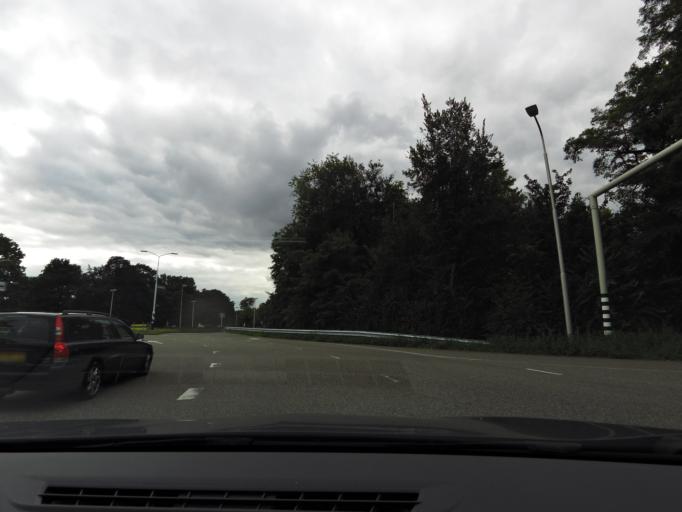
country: NL
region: Utrecht
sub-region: Gemeente Utrecht
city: Utrecht
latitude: 52.0965
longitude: 5.1437
